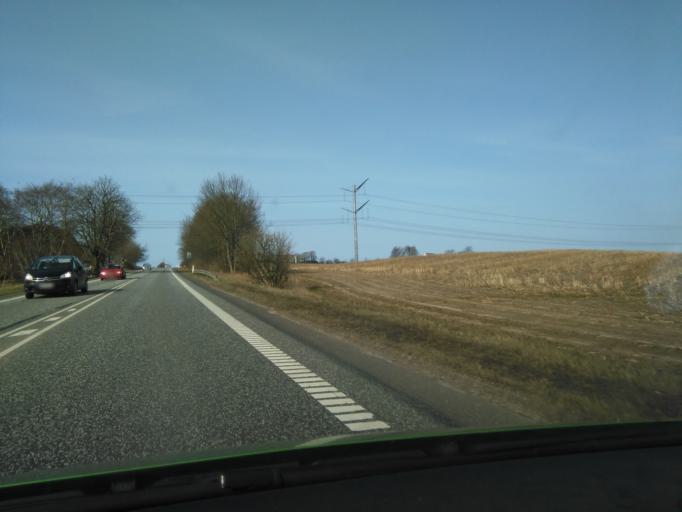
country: DK
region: Central Jutland
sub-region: Silkeborg Kommune
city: Kjellerup
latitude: 56.2514
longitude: 9.4515
